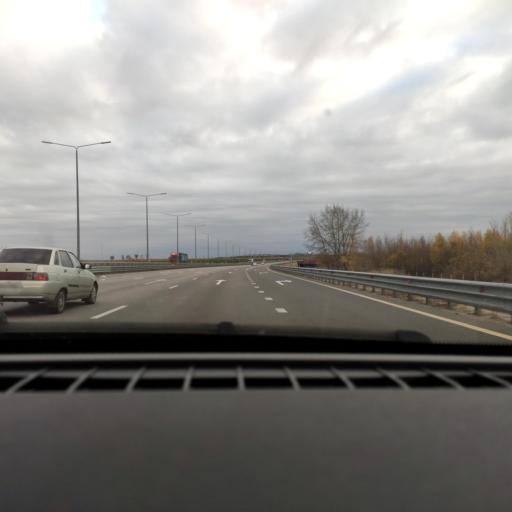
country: RU
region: Voronezj
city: Somovo
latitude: 51.7795
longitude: 39.2959
